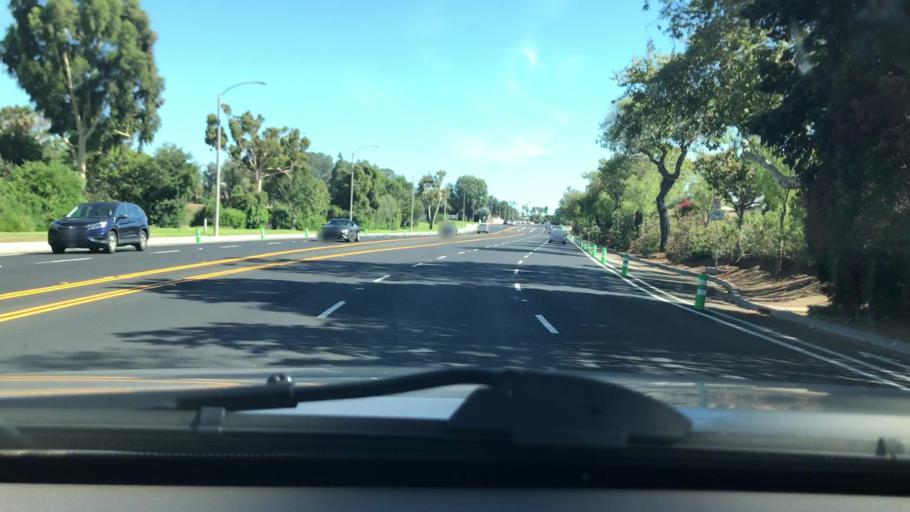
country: US
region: California
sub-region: Orange County
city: Rossmoor
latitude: 33.7847
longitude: -118.1225
